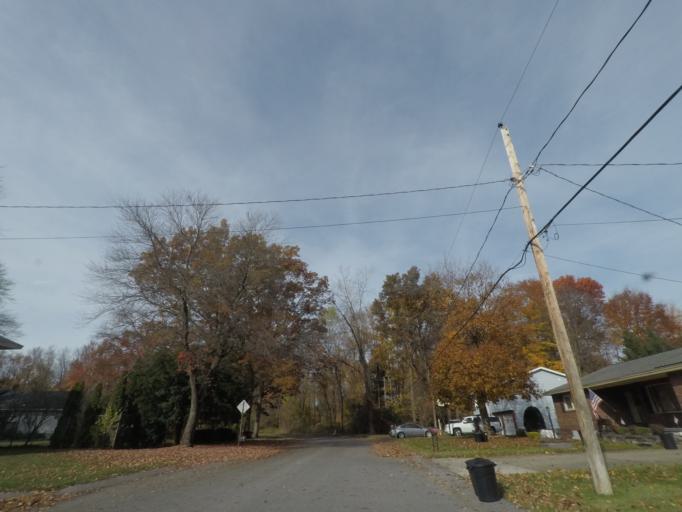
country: US
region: New York
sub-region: Schenectady County
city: Rotterdam
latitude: 42.7680
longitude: -73.9693
